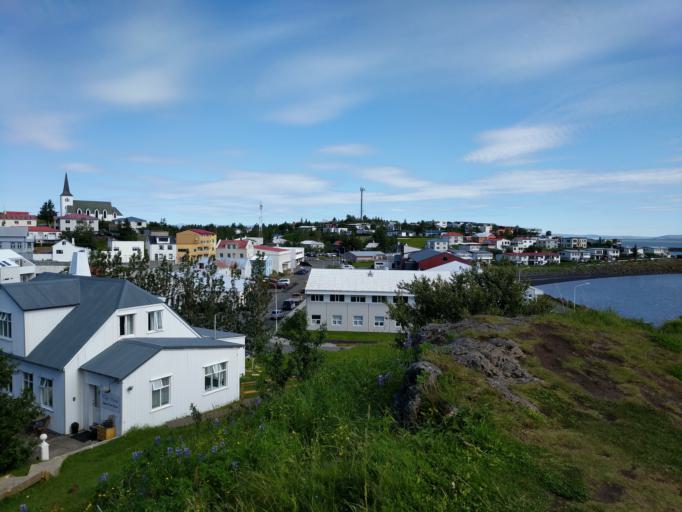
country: IS
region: West
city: Borgarnes
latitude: 64.5356
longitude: -21.9226
